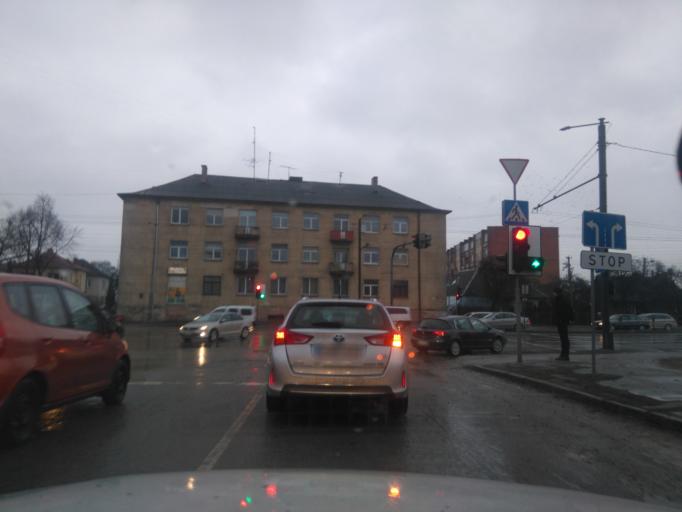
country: LT
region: Kauno apskritis
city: Dainava (Kaunas)
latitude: 54.8973
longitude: 23.9563
